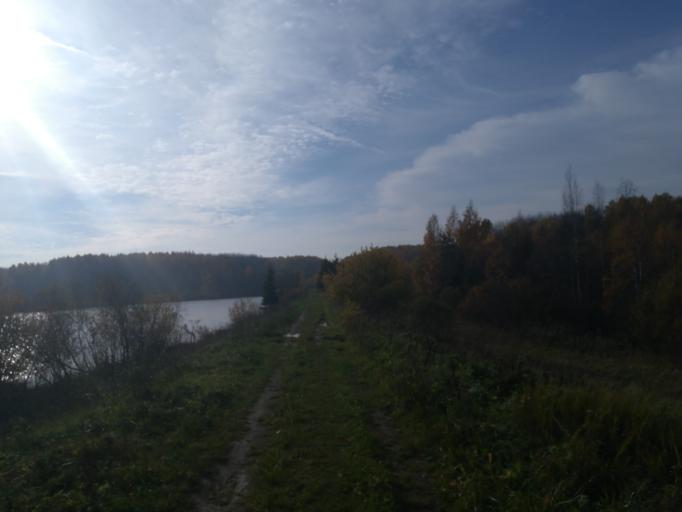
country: RU
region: Leningrad
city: Sista-Palkino
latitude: 59.5921
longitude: 28.8280
